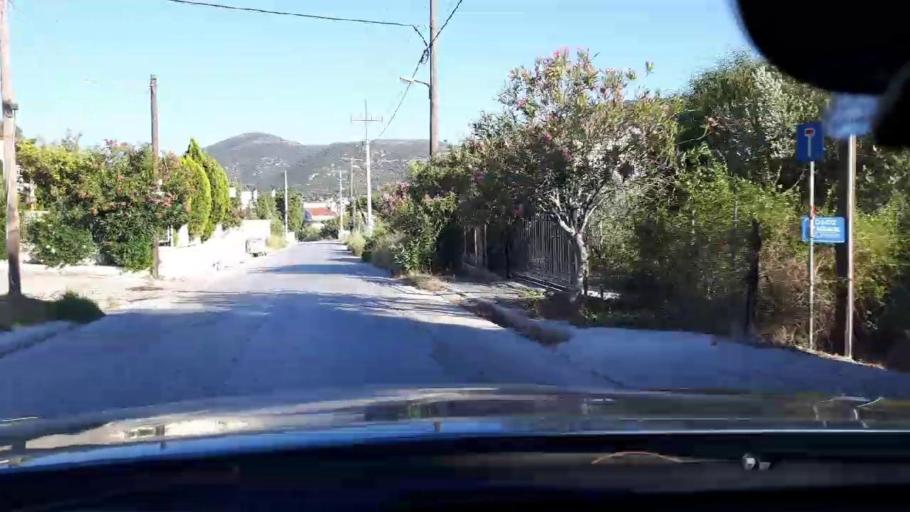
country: GR
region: Attica
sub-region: Nomarchia Anatolikis Attikis
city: Limin Mesoyaias
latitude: 37.8715
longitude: 24.0134
